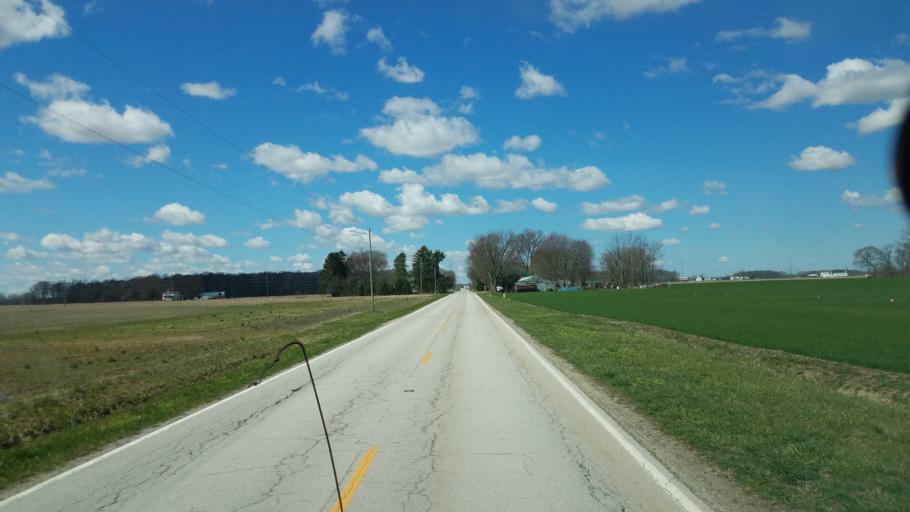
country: US
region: Ohio
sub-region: Sandusky County
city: Green Springs
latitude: 41.2567
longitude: -83.1056
